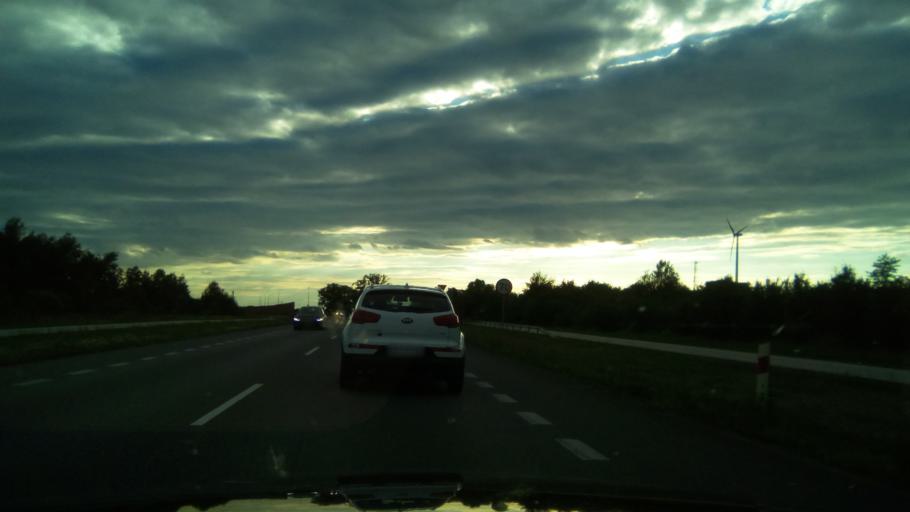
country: PL
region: Masovian Voivodeship
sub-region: Powiat zyrardowski
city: Mszczonow
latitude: 51.9811
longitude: 20.5327
